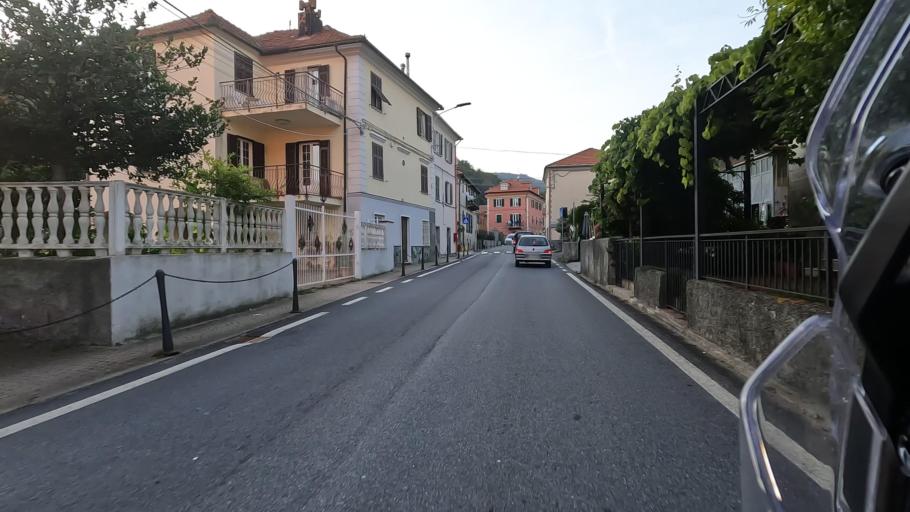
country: IT
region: Liguria
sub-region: Provincia di Savona
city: Osteria dei Cacciatori-Stella
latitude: 44.4166
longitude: 8.4818
